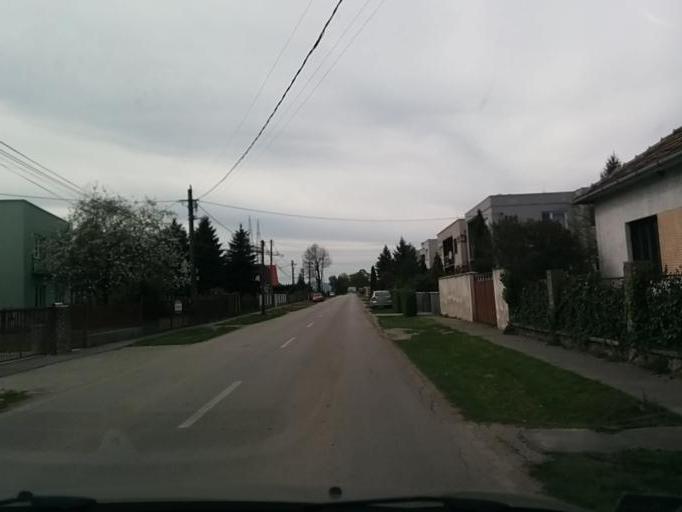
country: SK
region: Trnavsky
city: Sladkovicovo
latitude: 48.2351
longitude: 17.5650
